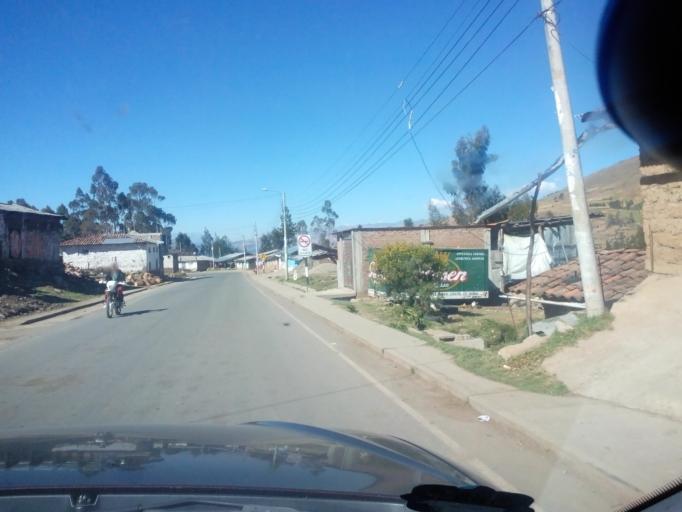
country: PE
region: Apurimac
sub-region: Provincia de Andahuaylas
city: Talavera
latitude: -13.6537
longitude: -73.5284
